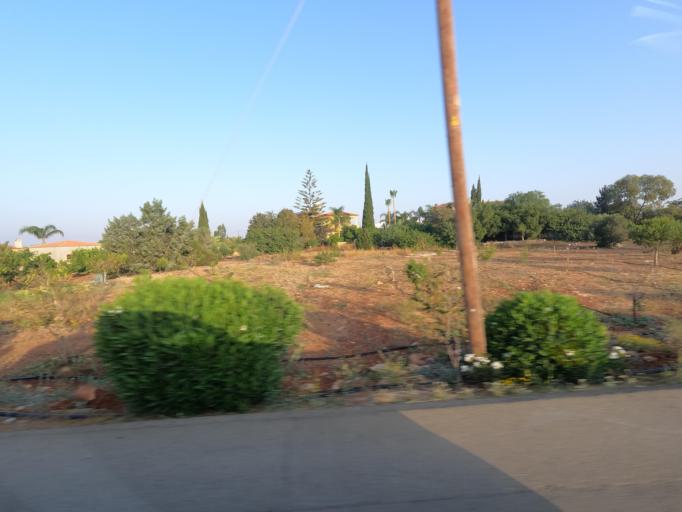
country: CY
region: Ammochostos
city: Frenaros
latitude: 35.0130
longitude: 33.9394
